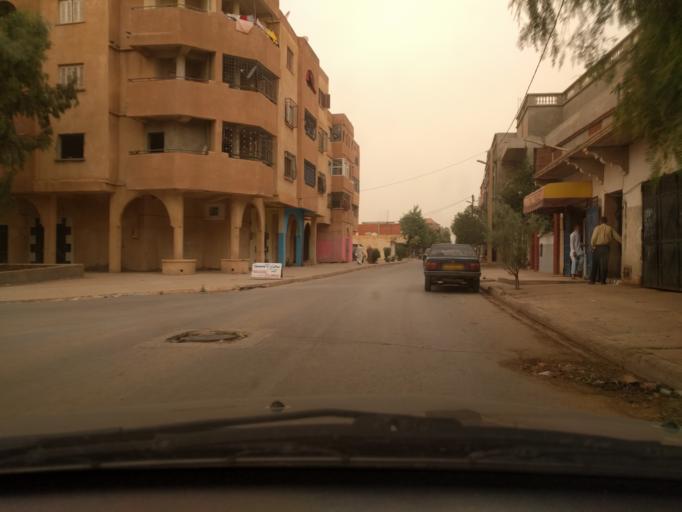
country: DZ
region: Tiaret
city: Frenda
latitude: 35.0639
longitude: 1.0631
